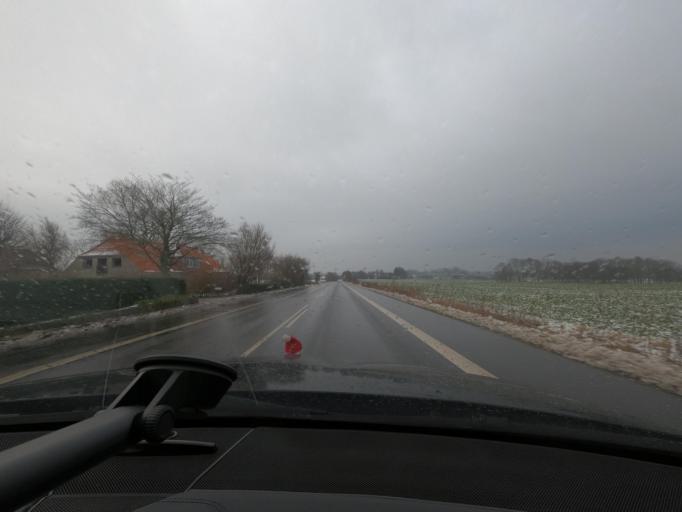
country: DK
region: South Denmark
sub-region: Sonderborg Kommune
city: Horuphav
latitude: 54.9009
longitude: 9.9535
